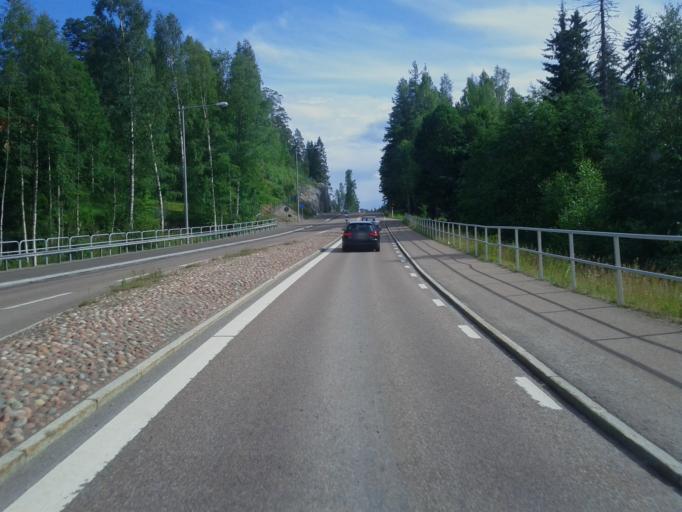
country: SE
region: Dalarna
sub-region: Faluns Kommun
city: Grycksbo
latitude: 60.6802
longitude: 15.5067
